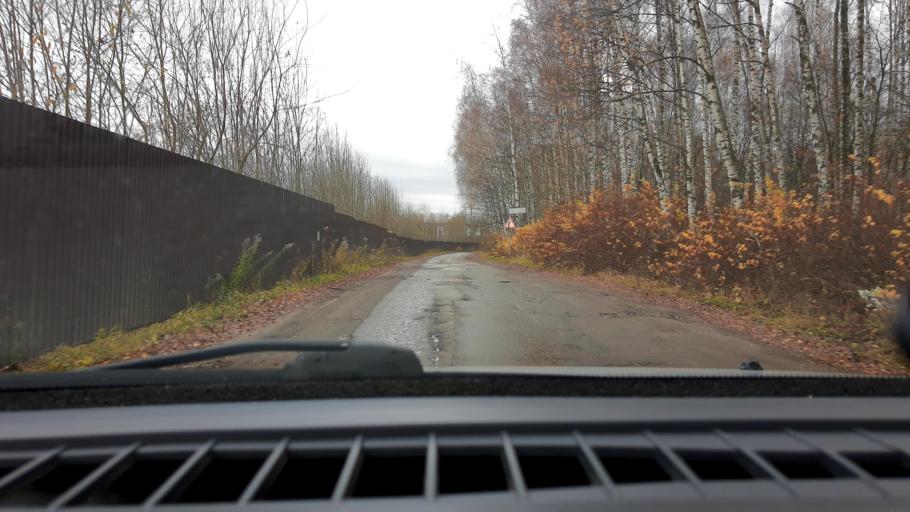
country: RU
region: Nizjnij Novgorod
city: Afonino
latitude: 56.1914
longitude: 44.1085
